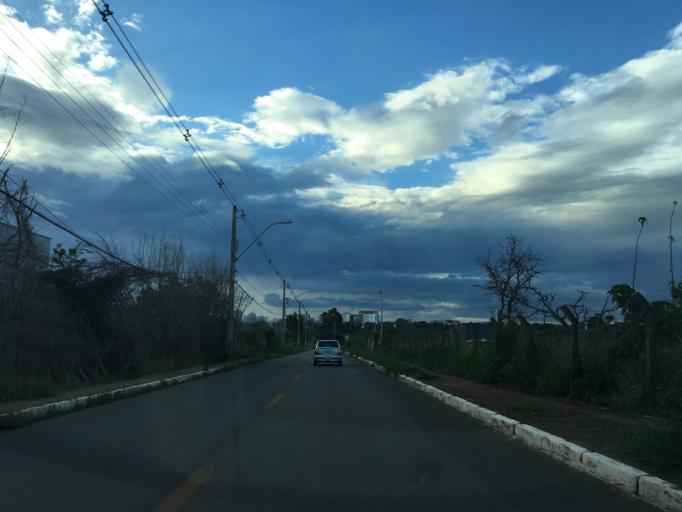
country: BR
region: Federal District
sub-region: Brasilia
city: Brasilia
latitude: -15.8149
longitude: -47.8460
